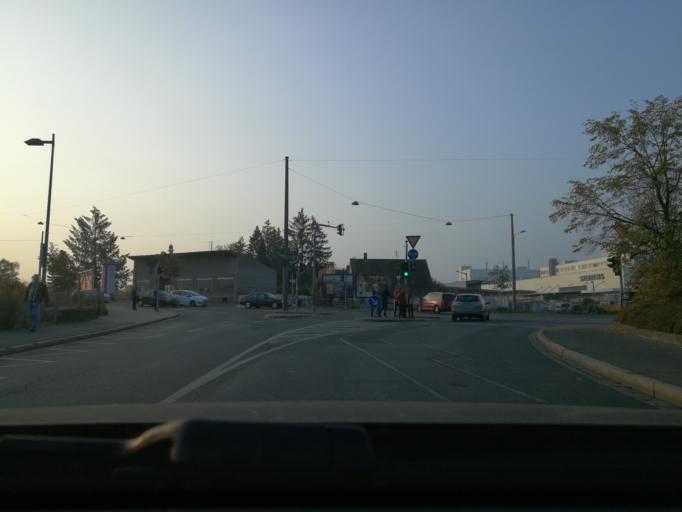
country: DE
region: Bavaria
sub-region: Regierungsbezirk Mittelfranken
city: Furth
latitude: 49.4831
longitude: 10.9662
